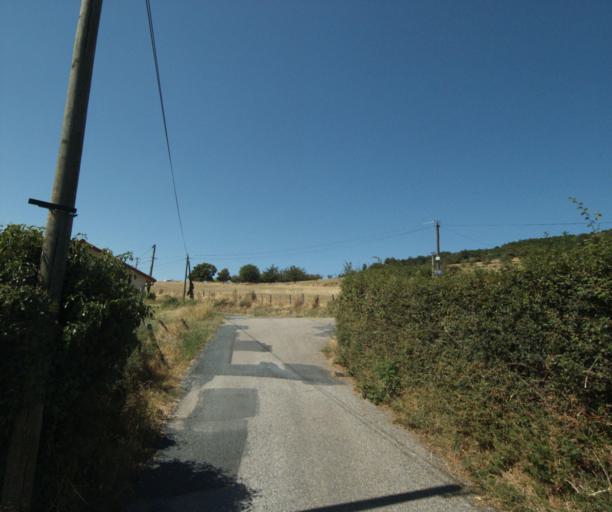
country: FR
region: Rhone-Alpes
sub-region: Departement du Rhone
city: Bessenay
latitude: 45.7954
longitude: 4.5441
